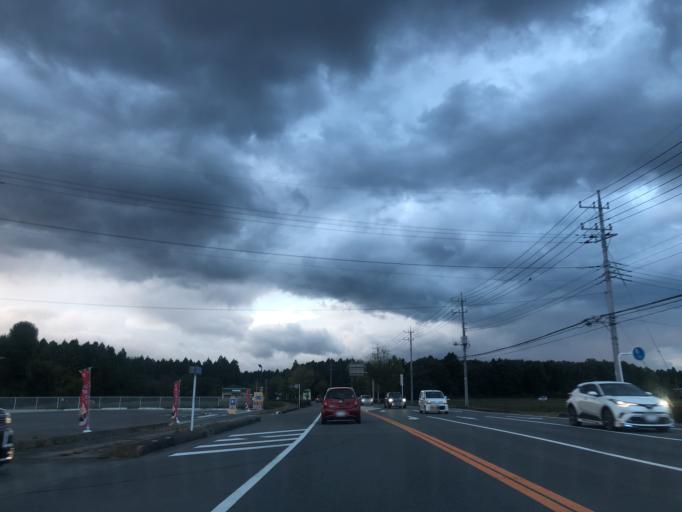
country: JP
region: Tochigi
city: Kuroiso
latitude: 36.9550
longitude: 140.0030
